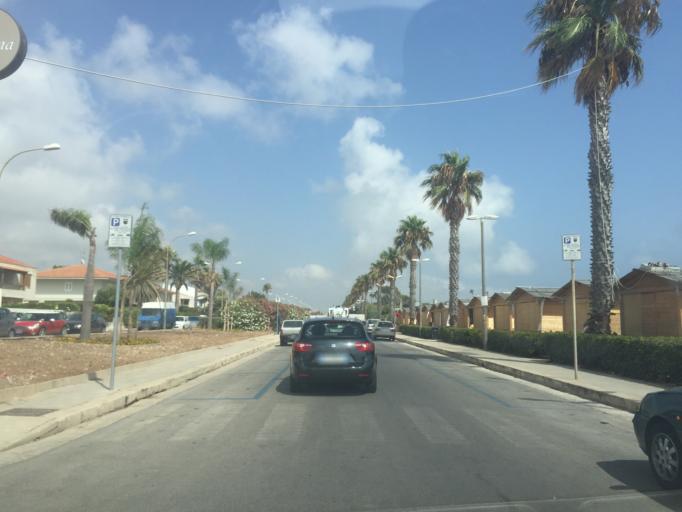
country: IT
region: Sicily
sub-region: Ragusa
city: Marina di Ragusa
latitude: 36.7814
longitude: 14.5641
